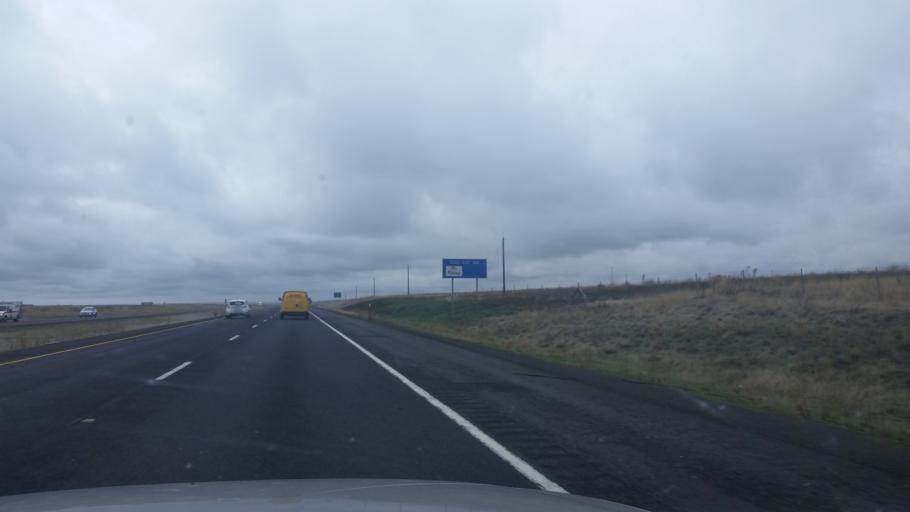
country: US
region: Washington
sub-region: Spokane County
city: Medical Lake
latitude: 47.3168
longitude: -117.9546
